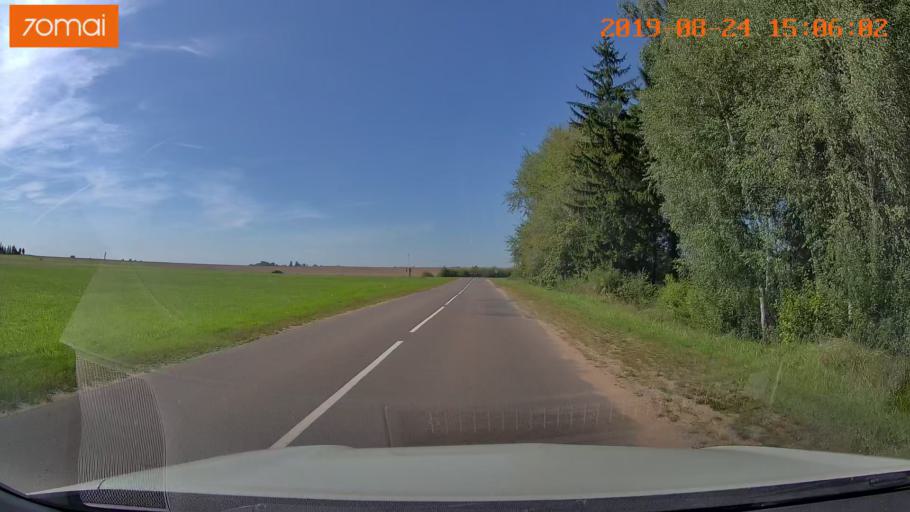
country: BY
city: Michanovichi
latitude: 53.5984
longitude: 27.6785
